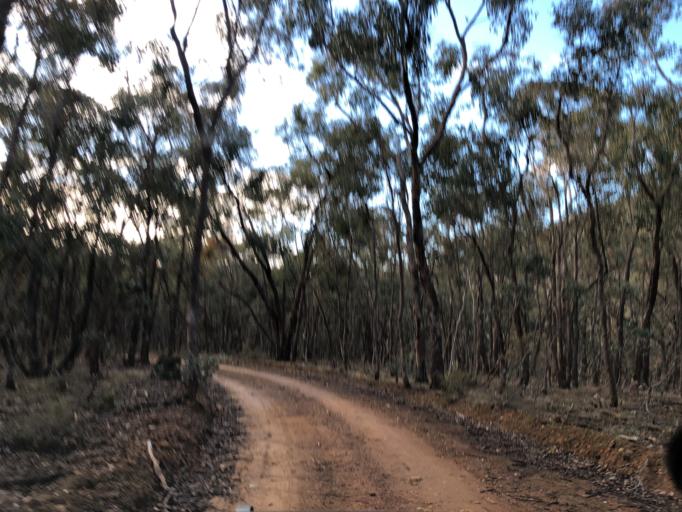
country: AU
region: Victoria
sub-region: Mount Alexander
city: Castlemaine
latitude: -37.2216
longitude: 144.2645
